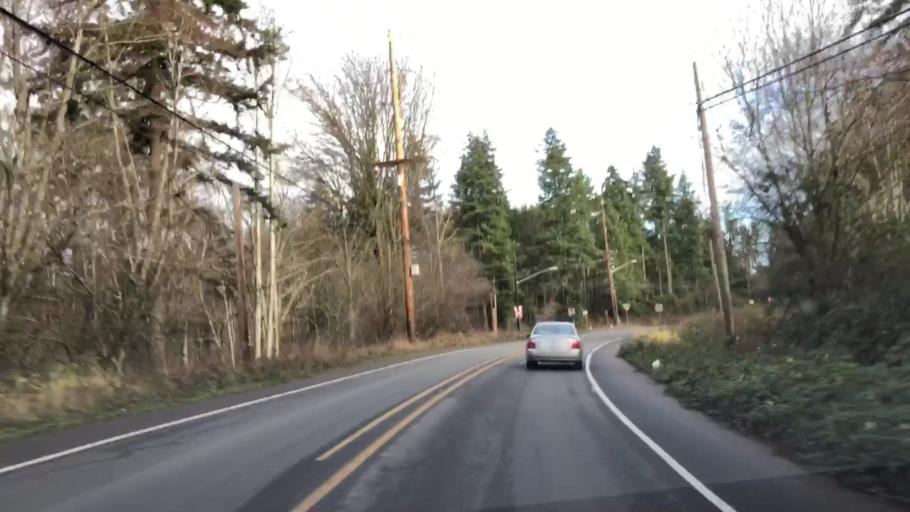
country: US
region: Washington
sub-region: Kitsap County
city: Suquamish
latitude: 47.7216
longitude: -122.5697
